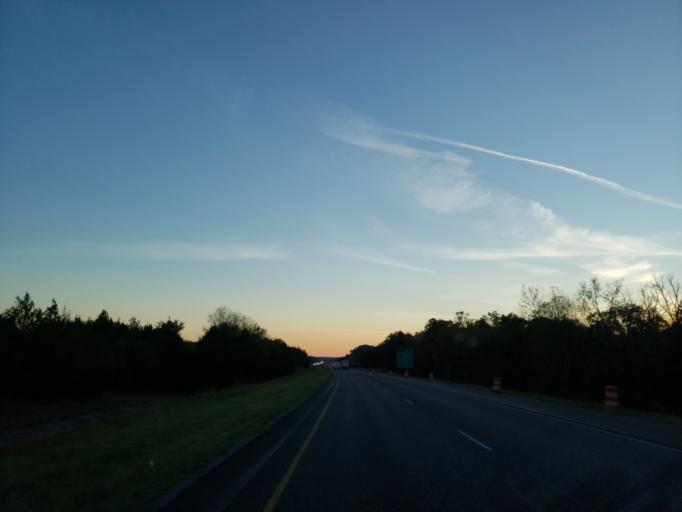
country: US
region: Alabama
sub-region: Sumter County
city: Livingston
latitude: 32.6441
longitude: -88.1977
